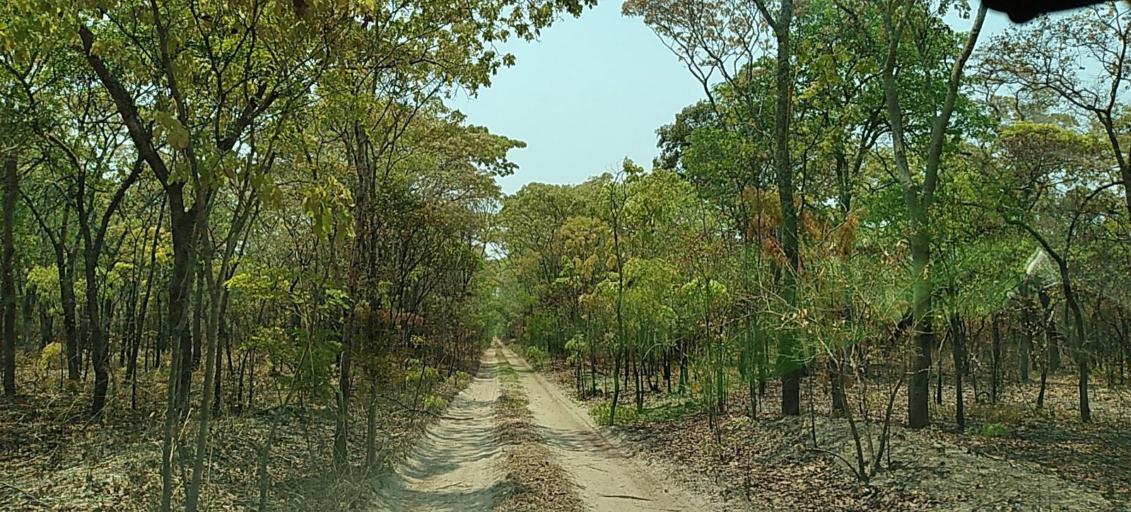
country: ZM
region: North-Western
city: Kabompo
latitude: -13.6567
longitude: 24.4637
